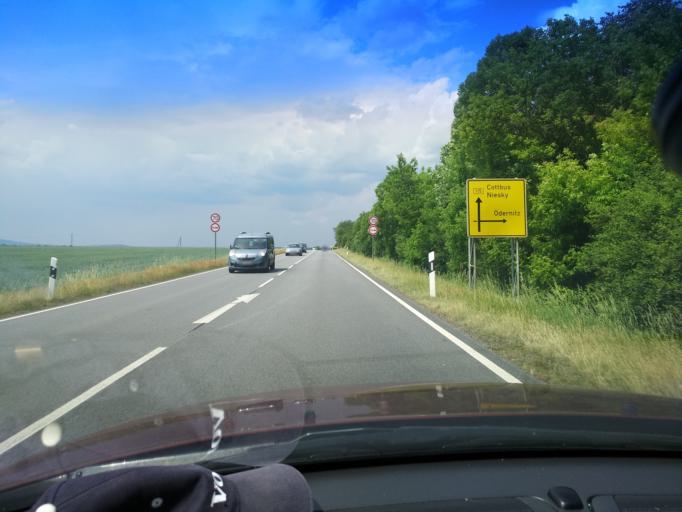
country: DE
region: Saxony
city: Niesky
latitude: 51.2668
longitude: 14.8537
